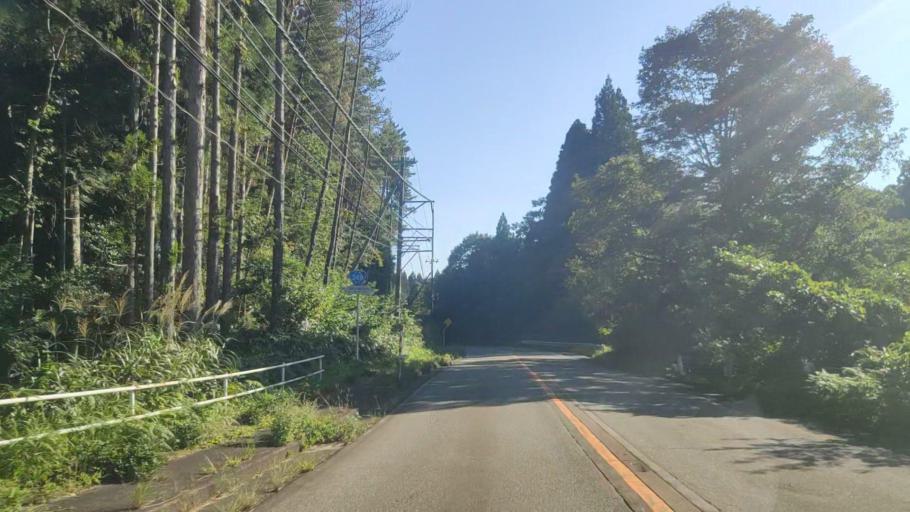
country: JP
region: Ishikawa
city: Nanao
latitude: 37.1287
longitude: 136.8636
